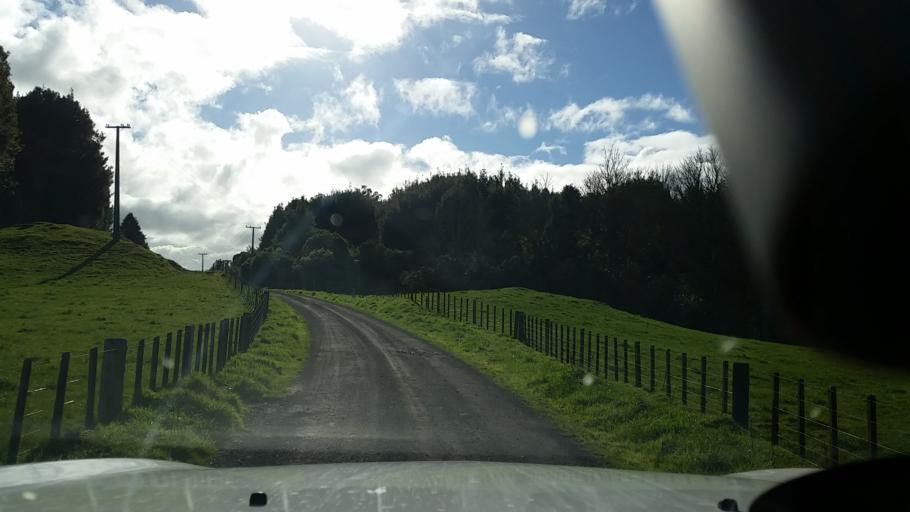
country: NZ
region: Bay of Plenty
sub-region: Rotorua District
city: Rotorua
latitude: -38.1034
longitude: 176.0693
